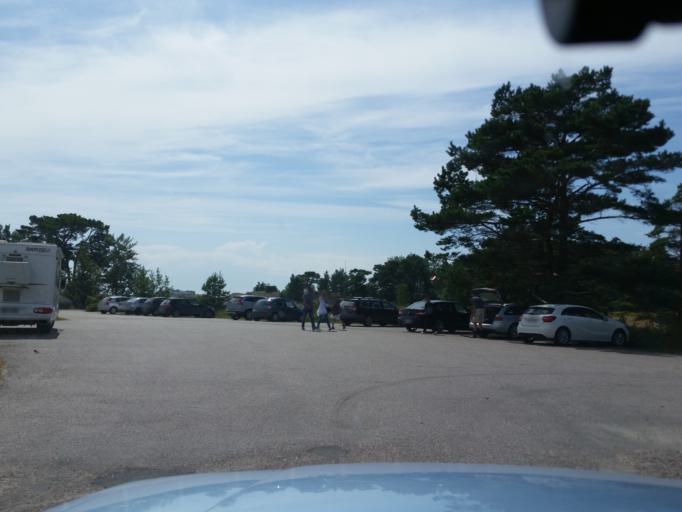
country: FI
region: Uusimaa
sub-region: Raaseporin
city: Hanko
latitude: 59.8249
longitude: 23.0076
